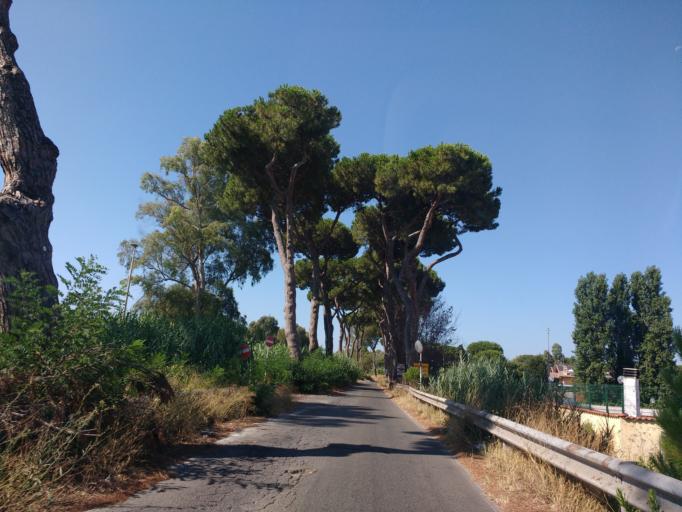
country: IT
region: Latium
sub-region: Citta metropolitana di Roma Capitale
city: Acilia-Castel Fusano-Ostia Antica
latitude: 41.7465
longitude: 12.3236
